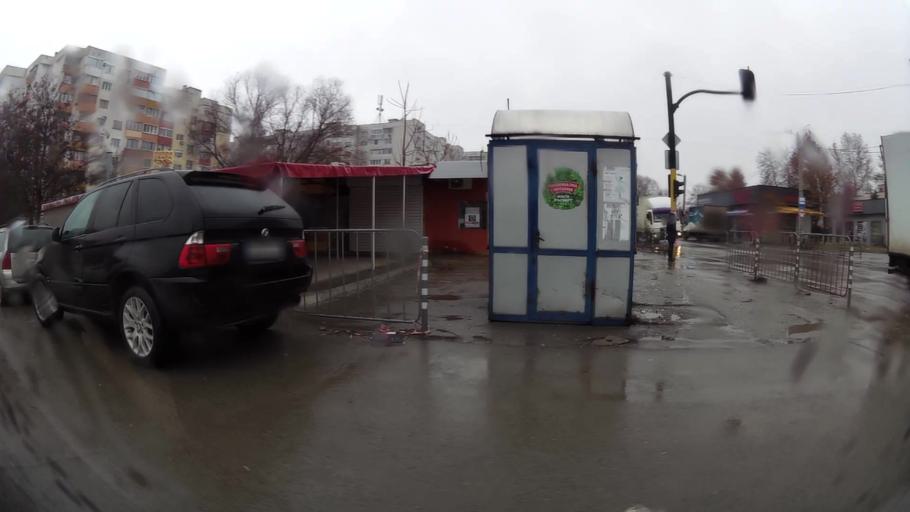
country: BG
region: Sofia-Capital
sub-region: Stolichna Obshtina
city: Sofia
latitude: 42.6437
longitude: 23.4124
